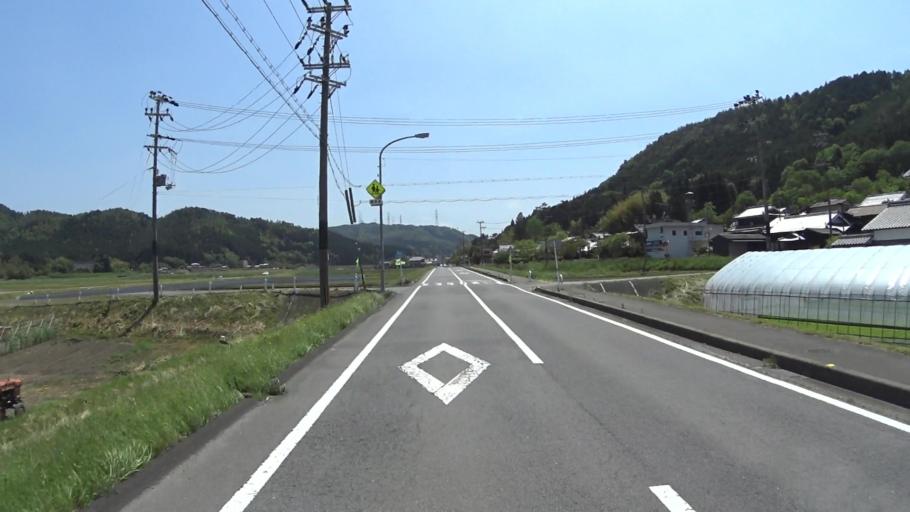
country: JP
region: Kyoto
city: Kameoka
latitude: 35.0211
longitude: 135.4876
